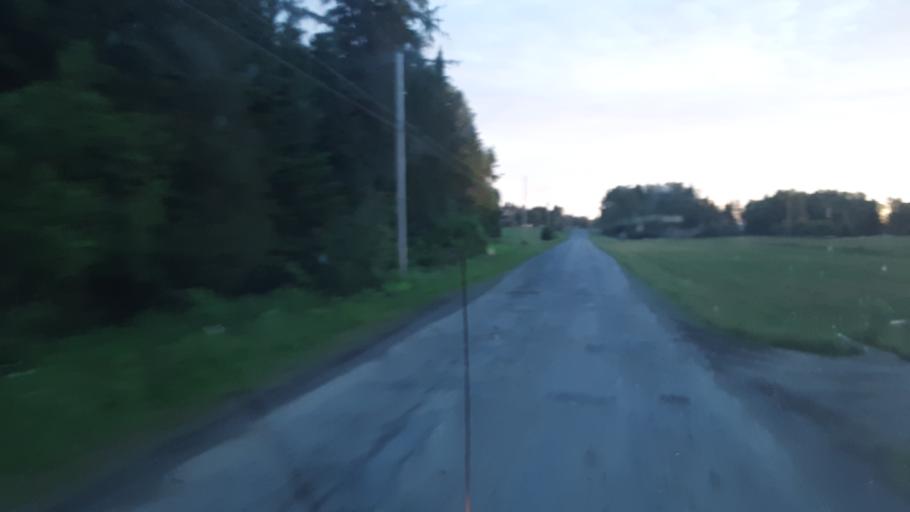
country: US
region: Maine
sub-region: Aroostook County
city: Caribou
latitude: 46.8661
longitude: -68.0922
